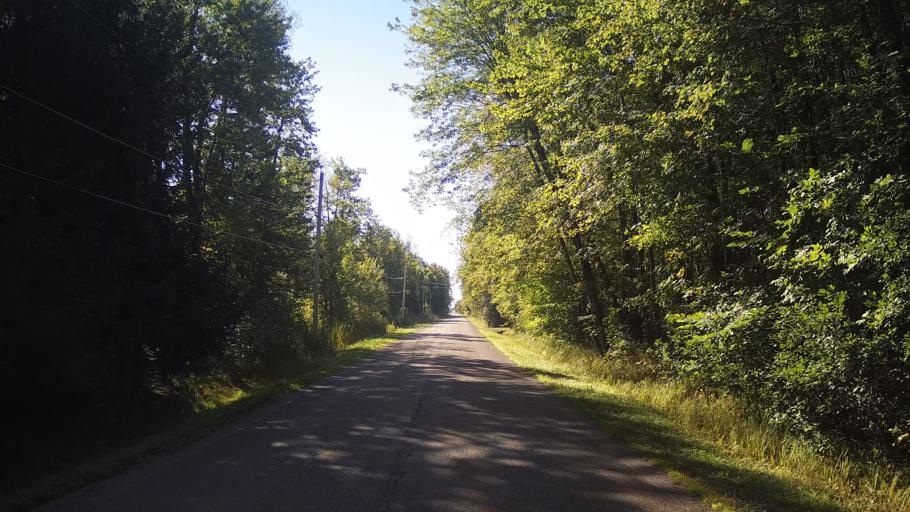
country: CA
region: Ontario
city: Prescott
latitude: 44.9843
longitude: -75.5812
